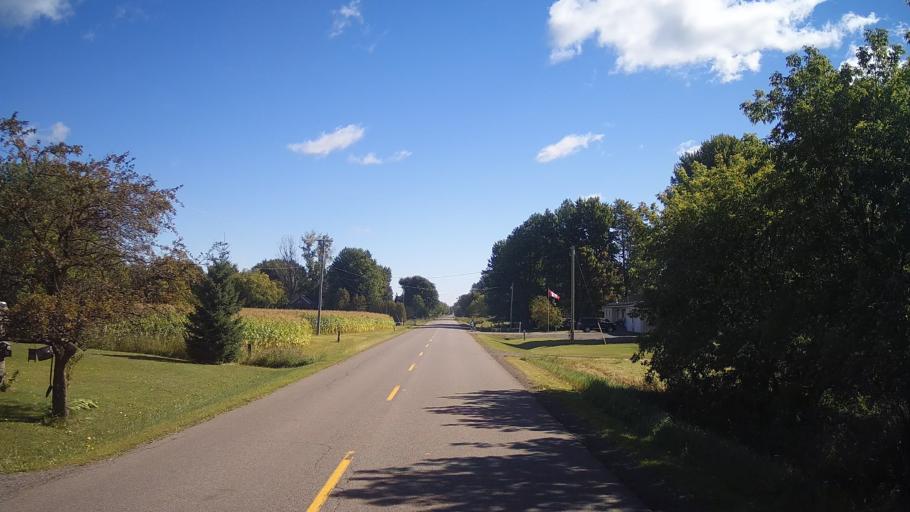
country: CA
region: Ontario
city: Prescott
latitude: 44.9042
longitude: -75.3930
